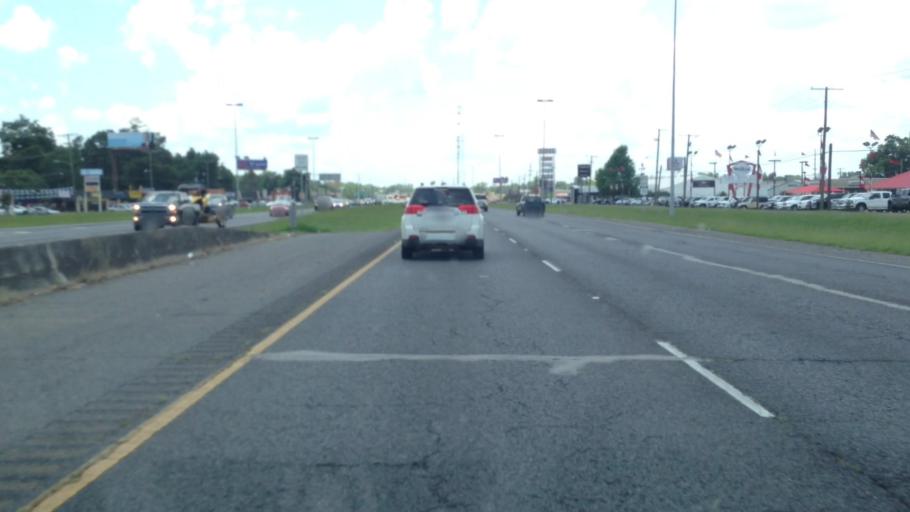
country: US
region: Louisiana
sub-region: Rapides Parish
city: Alexandria
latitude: 31.2829
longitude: -92.4736
